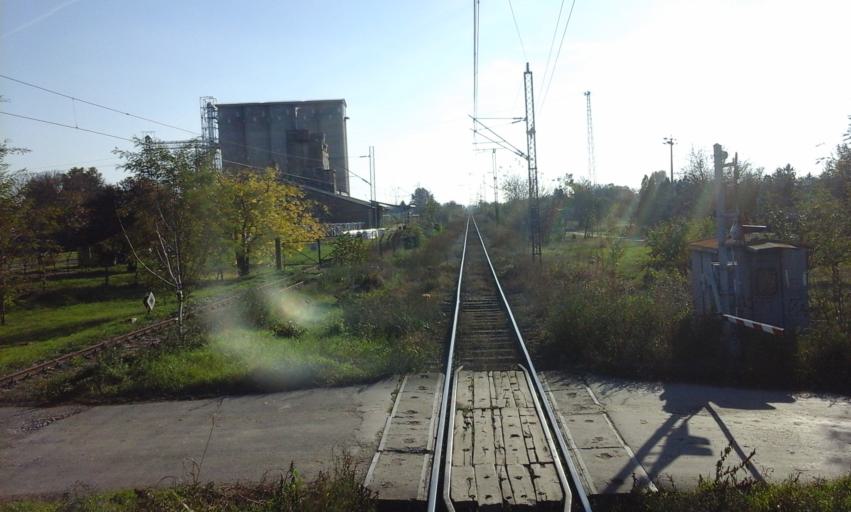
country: RS
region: Autonomna Pokrajina Vojvodina
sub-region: Severnobacki Okrug
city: Backa Topola
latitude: 45.8107
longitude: 19.6485
